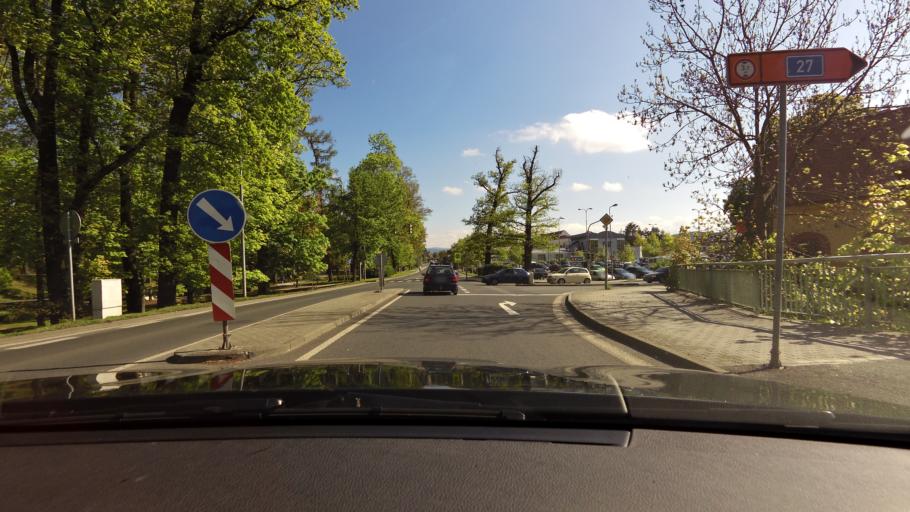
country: CZ
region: Plzensky
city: Klatovy
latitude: 49.3896
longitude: 13.2962
